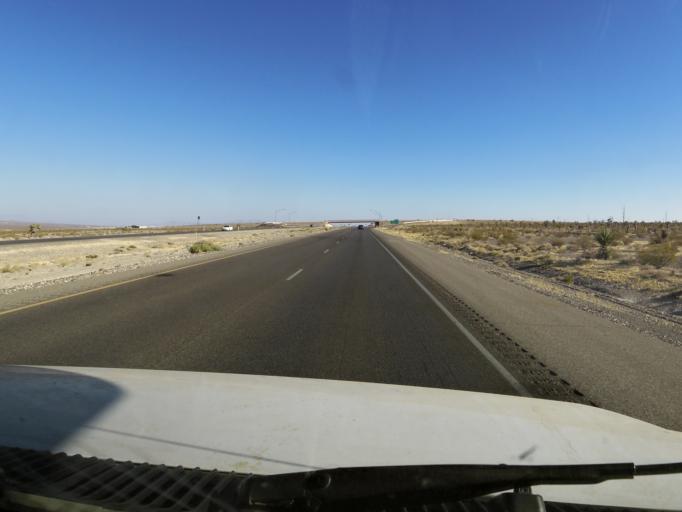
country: US
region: Nevada
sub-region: Clark County
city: Summerlin South
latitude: 36.3671
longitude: -115.3577
